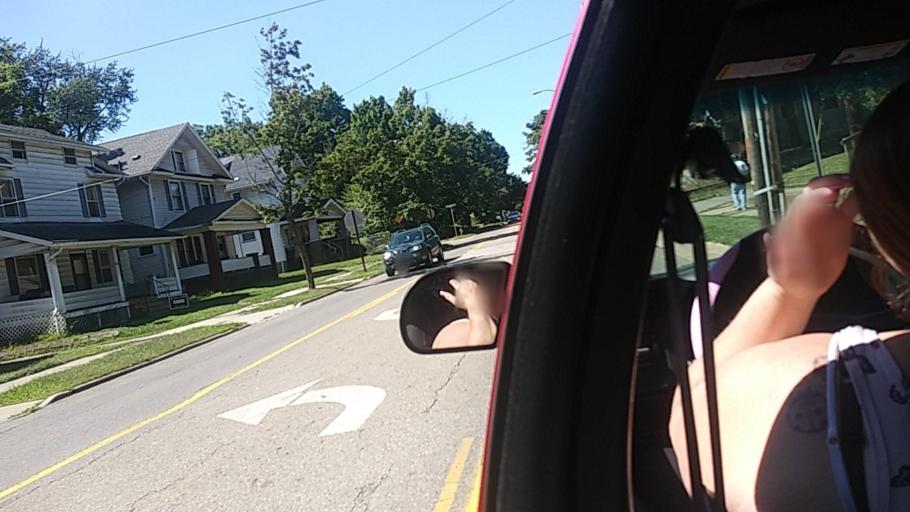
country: US
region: Ohio
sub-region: Summit County
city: Akron
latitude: 41.0945
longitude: -81.5491
